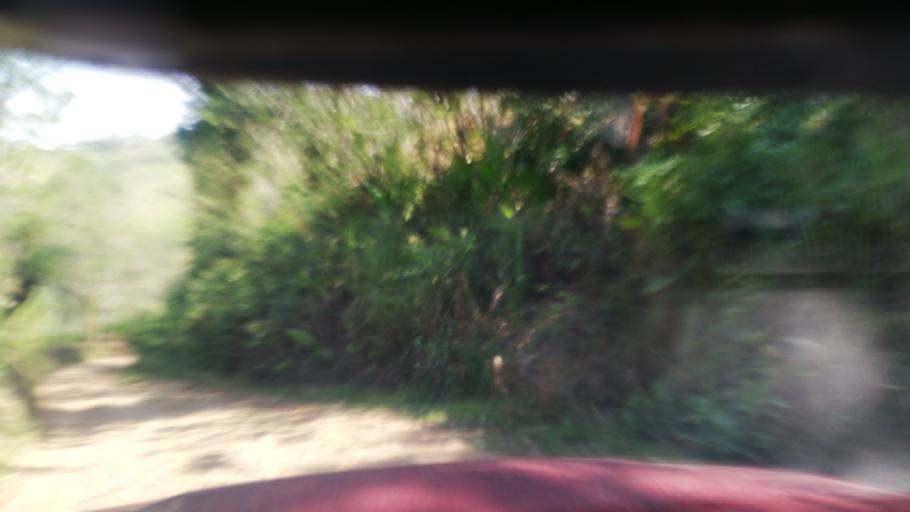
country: CO
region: Risaralda
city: Balboa
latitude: 4.9032
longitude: -75.9402
